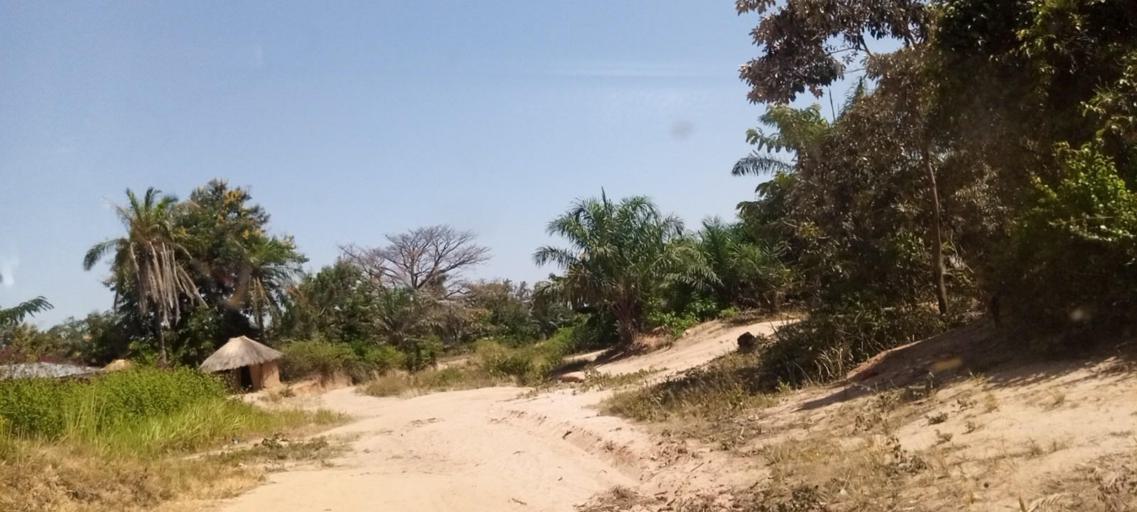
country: CD
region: Kasai-Oriental
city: Kabinda
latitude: -5.9554
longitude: 24.8020
